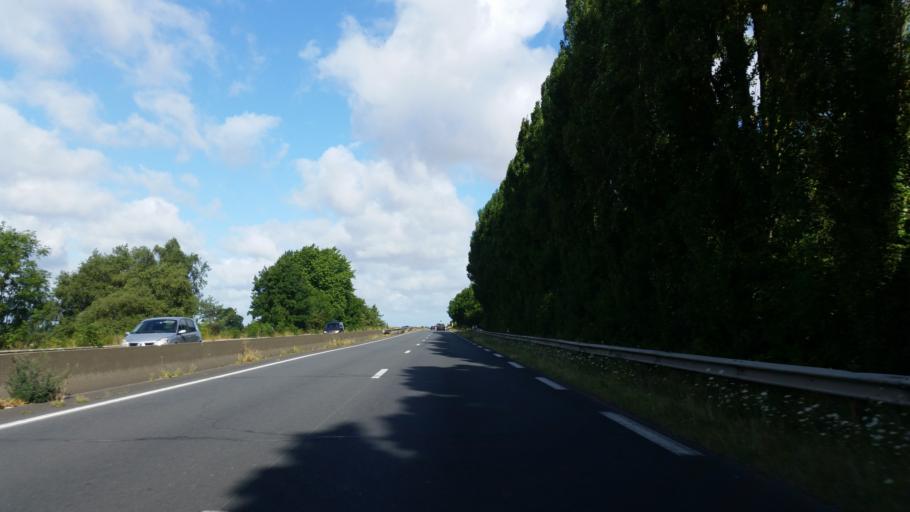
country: FR
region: Lower Normandy
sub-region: Departement du Calvados
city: Saint-Manvieu
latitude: 49.2121
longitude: -0.5218
